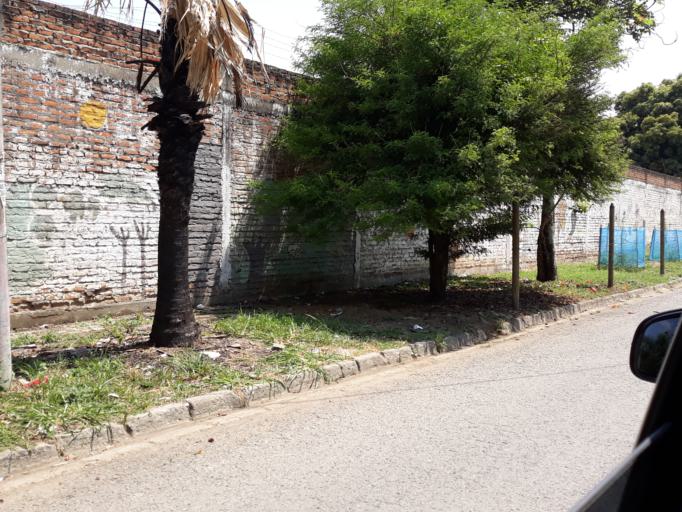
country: CO
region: Valle del Cauca
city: Cali
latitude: 3.4811
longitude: -76.5014
